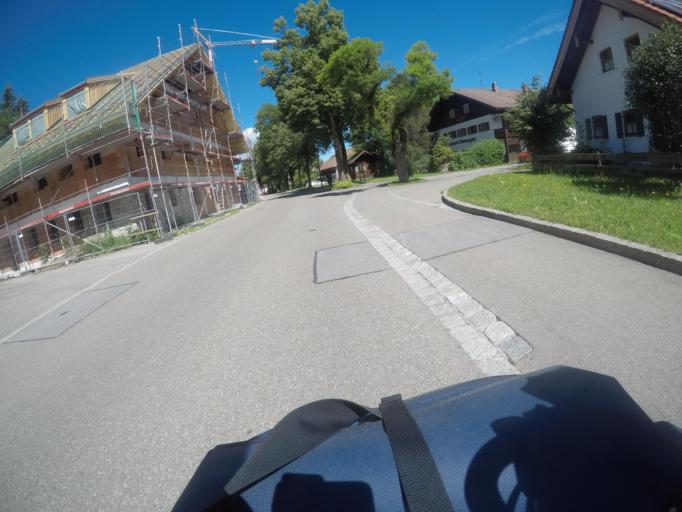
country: DE
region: Bavaria
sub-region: Swabia
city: Schwangau
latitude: 47.5790
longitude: 10.7370
